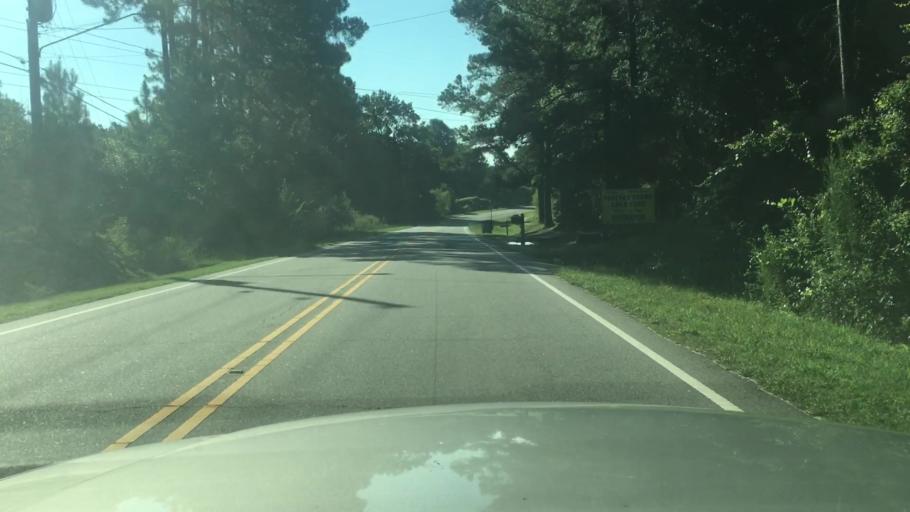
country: US
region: North Carolina
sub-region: Cumberland County
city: Fayetteville
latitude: 35.1266
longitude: -78.8902
